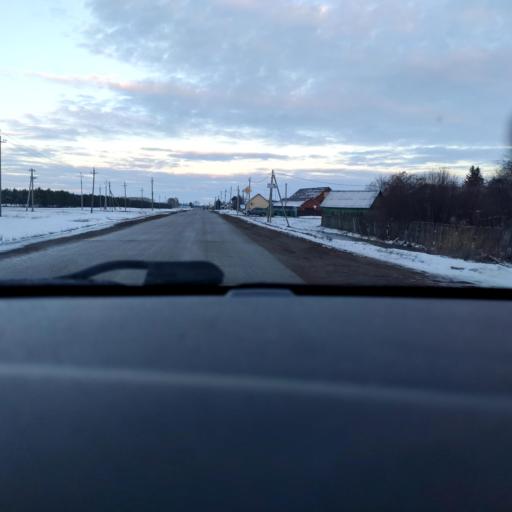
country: RU
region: Bashkortostan
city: Kushnarenkovo
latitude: 55.0966
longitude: 55.3578
